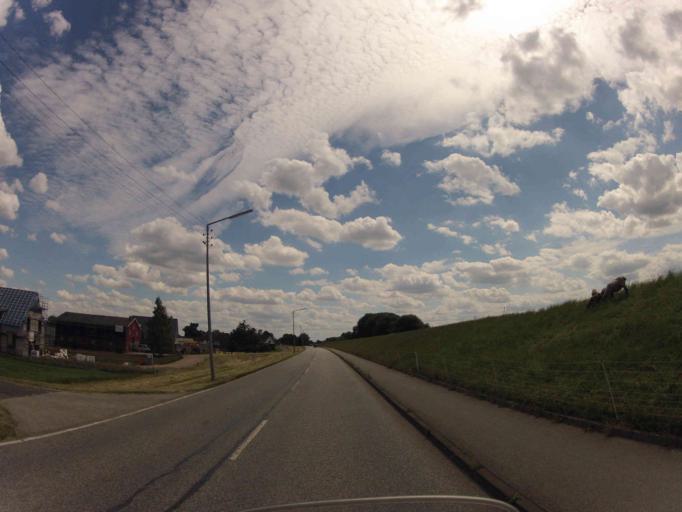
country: DE
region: Hamburg
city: Rothenburgsort
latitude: 53.4764
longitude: 10.0632
